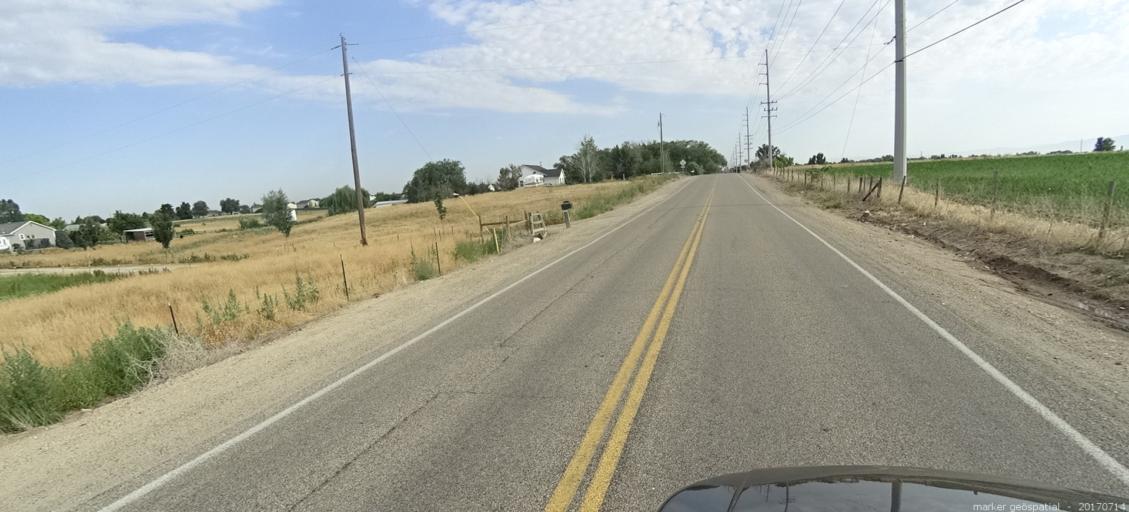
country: US
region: Idaho
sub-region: Ada County
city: Kuna
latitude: 43.4744
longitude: -116.4137
